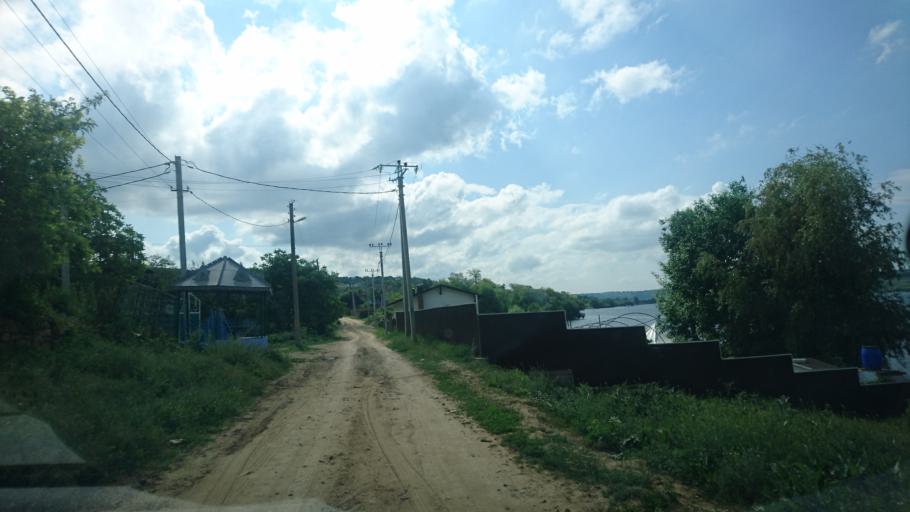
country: MD
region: Telenesti
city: Cocieri
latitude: 47.3620
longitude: 29.1002
